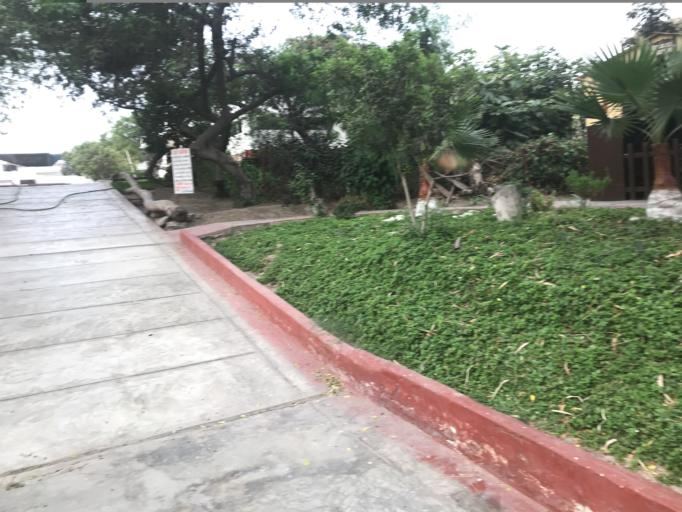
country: PE
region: Lima
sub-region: Lima
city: Urb. Santo Domingo
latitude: -11.9239
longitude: -77.0396
